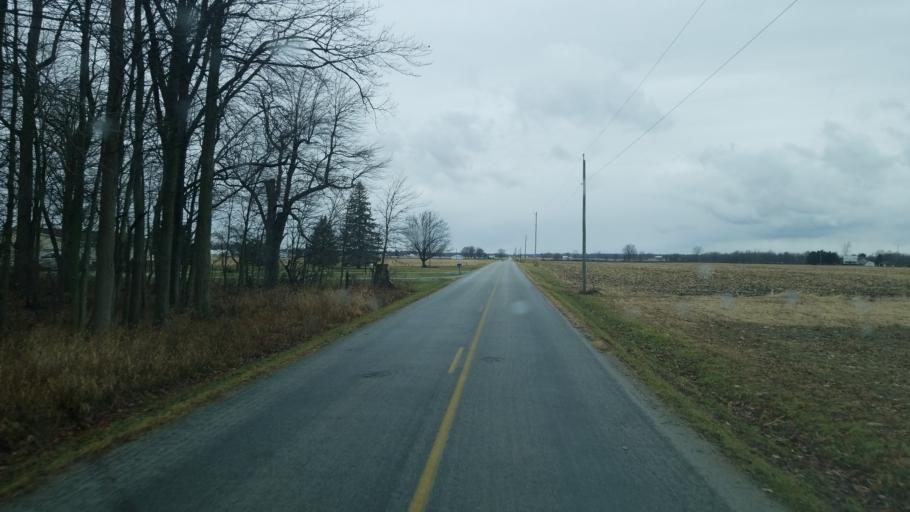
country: US
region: Ohio
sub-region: Hardin County
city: Kenton
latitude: 40.7023
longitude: -83.5662
